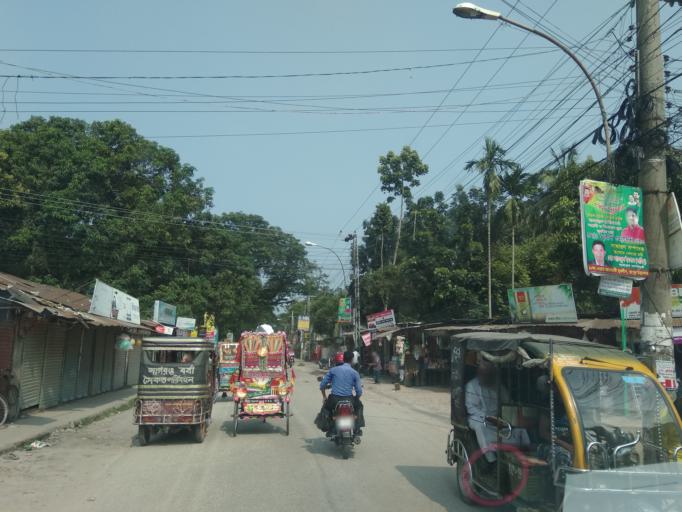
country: BD
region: Rangpur Division
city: Rangpur
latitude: 25.7585
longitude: 89.2348
